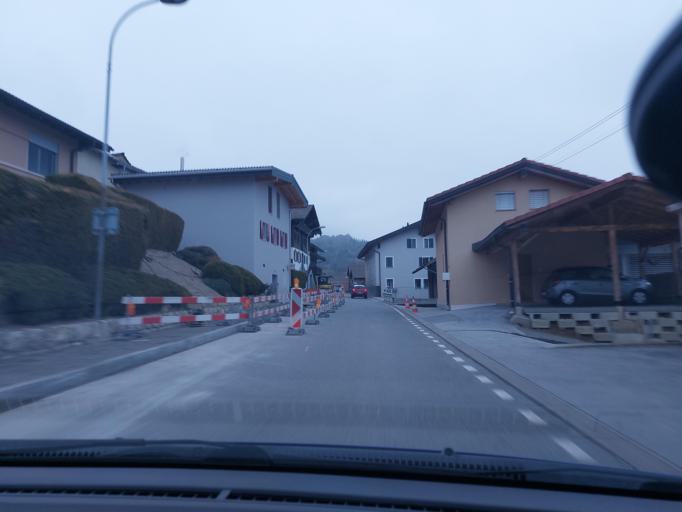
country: CH
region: Valais
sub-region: Sion District
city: Saviese
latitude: 46.2582
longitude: 7.3647
